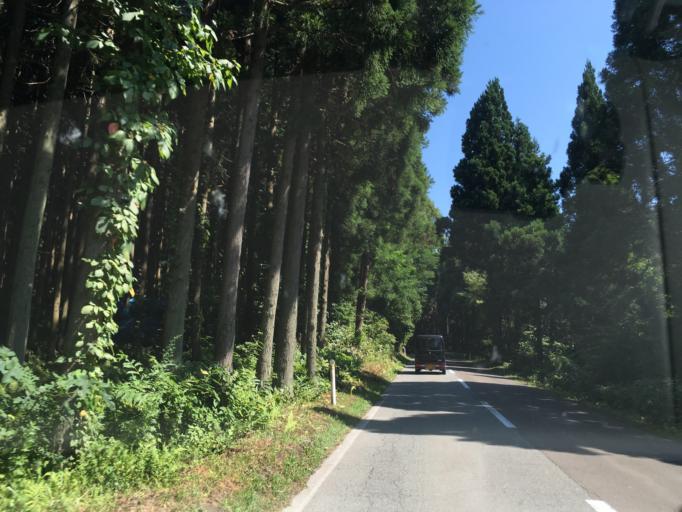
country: JP
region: Akita
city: Tenno
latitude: 39.9324
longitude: 139.8893
